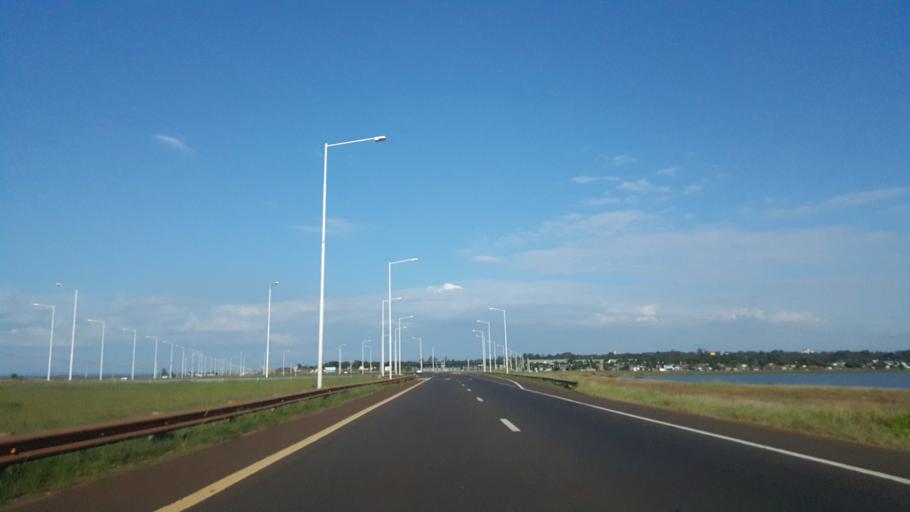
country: AR
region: Misiones
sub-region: Departamento de Capital
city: Posadas
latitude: -27.4121
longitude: -55.8894
